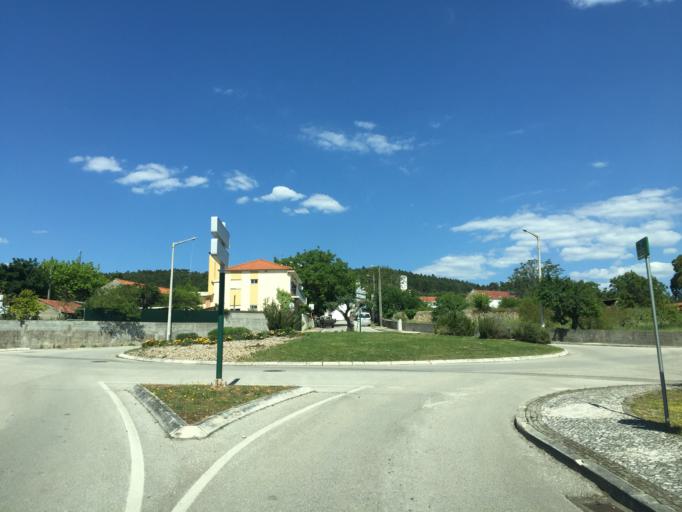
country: PT
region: Leiria
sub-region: Alvaiazere
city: Alvaiazere
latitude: 39.8249
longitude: -8.3848
